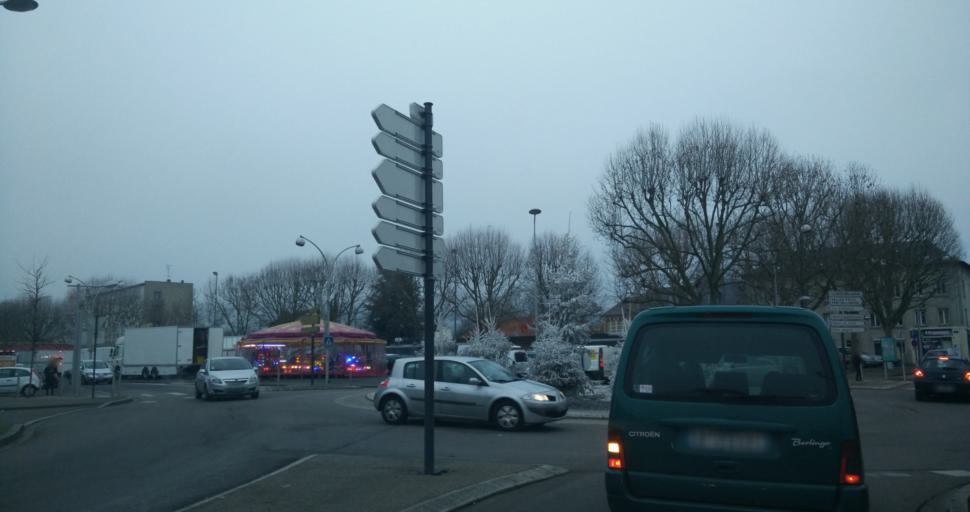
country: FR
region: Haute-Normandie
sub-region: Departement de l'Eure
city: Louviers
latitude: 49.2102
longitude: 1.1659
